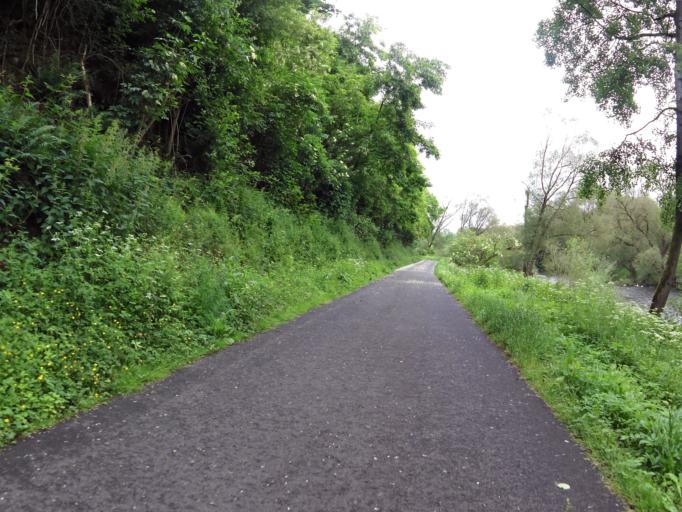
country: DE
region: Hesse
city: Breitenbach
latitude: 50.9596
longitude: 9.7813
